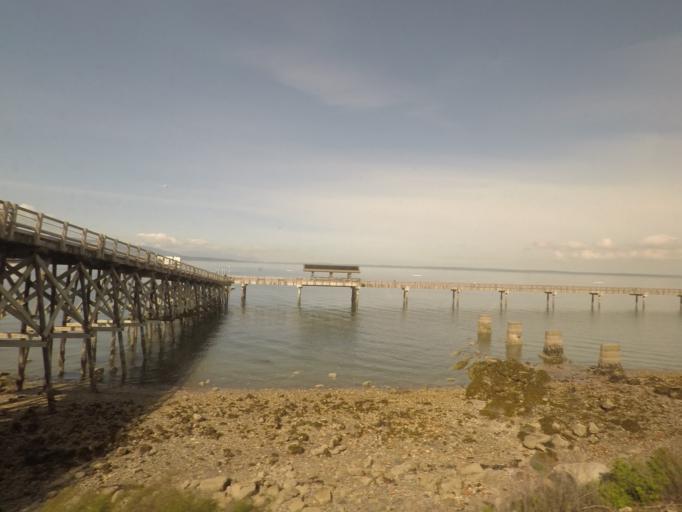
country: US
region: Washington
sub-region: Whatcom County
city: Bellingham
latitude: 48.7256
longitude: -122.5059
